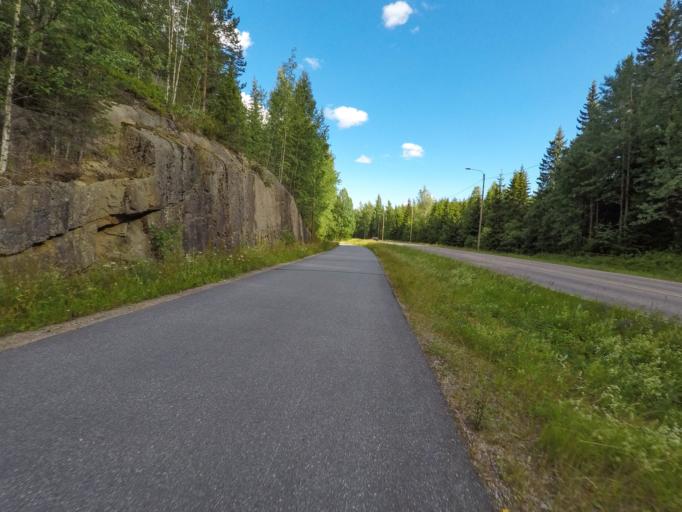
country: FI
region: South Karelia
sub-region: Lappeenranta
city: Lappeenranta
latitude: 61.1030
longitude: 28.1245
